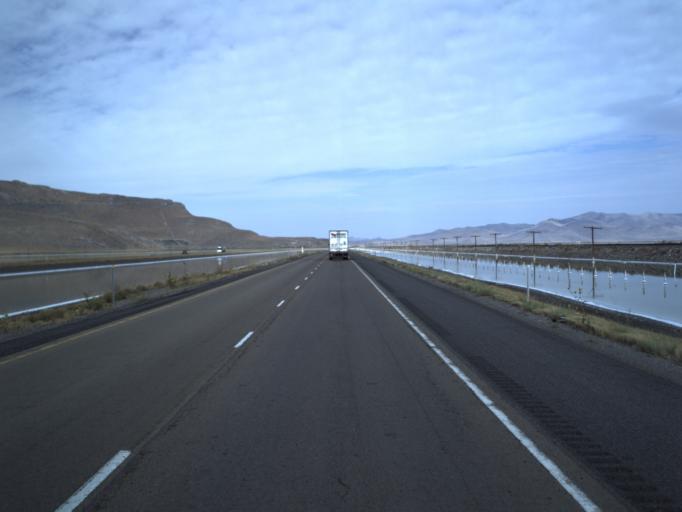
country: US
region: Utah
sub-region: Tooele County
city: Grantsville
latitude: 40.7318
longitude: -112.5933
